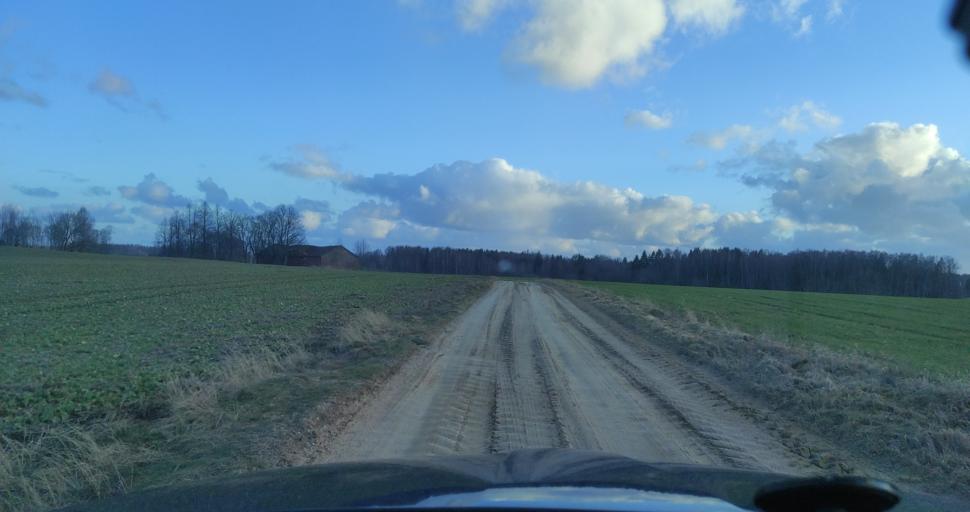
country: LV
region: Aizpute
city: Aizpute
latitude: 56.8680
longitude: 21.7590
